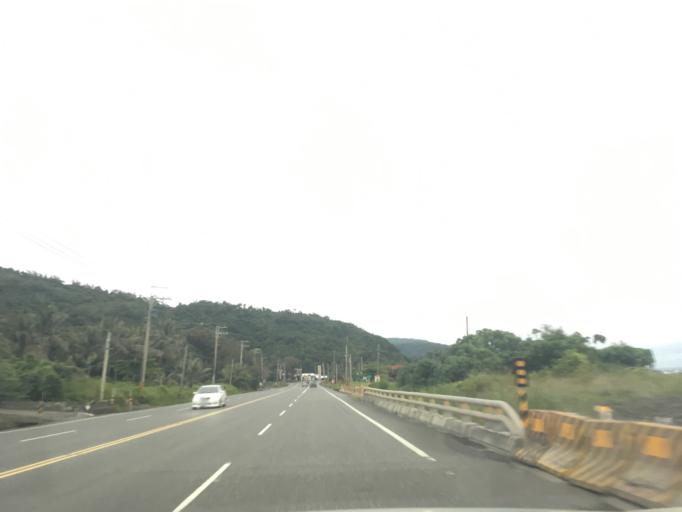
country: TW
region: Taiwan
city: Hengchun
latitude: 22.3270
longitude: 120.8922
